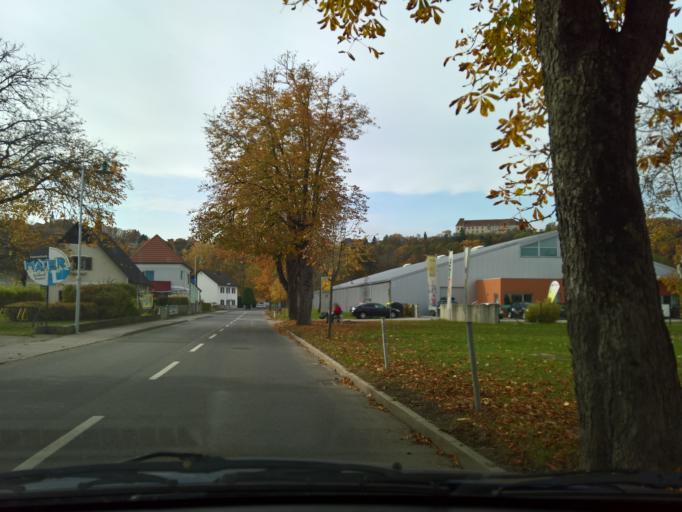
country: AT
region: Styria
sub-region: Politischer Bezirk Leibnitz
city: Leibnitz
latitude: 46.7800
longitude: 15.5304
